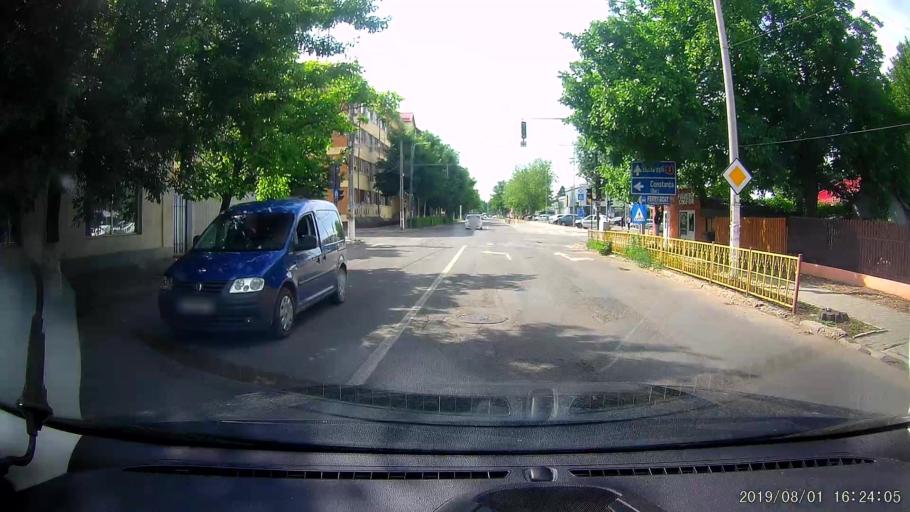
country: RO
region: Calarasi
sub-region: Municipiul Calarasi
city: Calarasi
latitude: 44.1972
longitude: 27.3315
